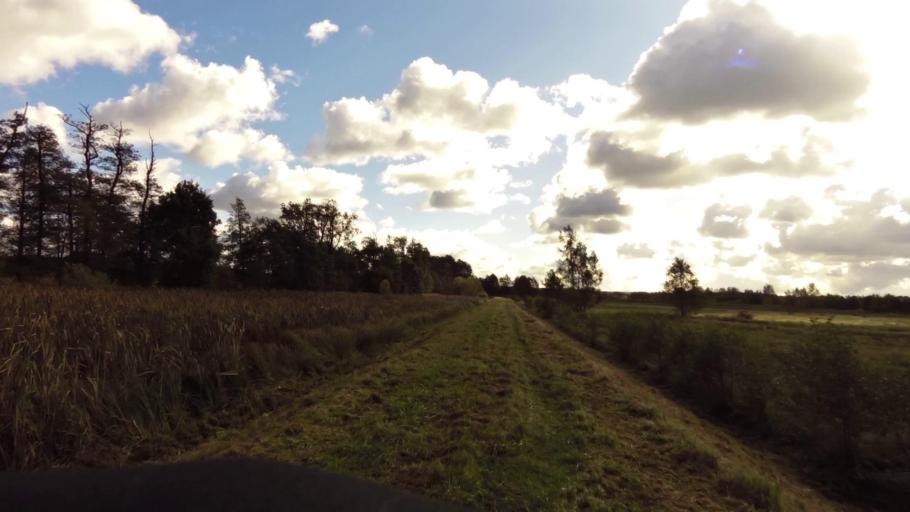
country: PL
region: West Pomeranian Voivodeship
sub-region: Powiat bialogardzki
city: Bialogard
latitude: 54.0017
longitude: 16.0124
